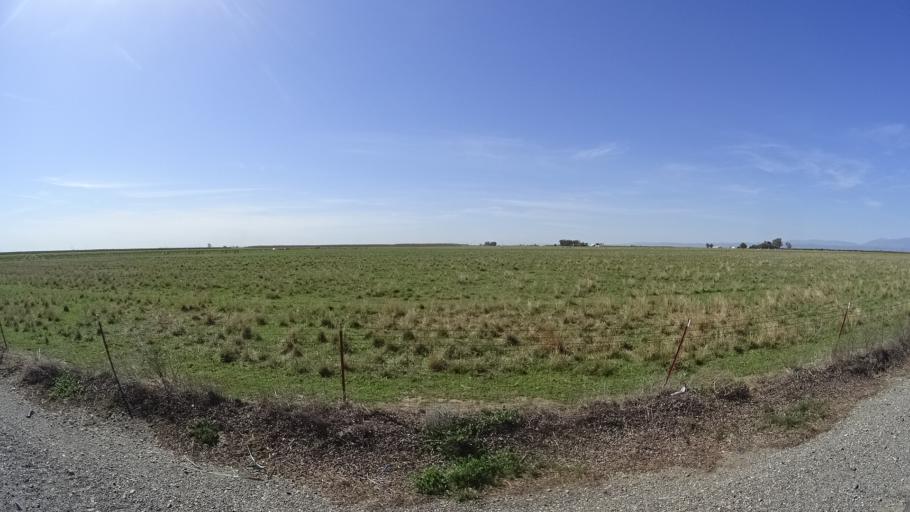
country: US
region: California
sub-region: Glenn County
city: Willows
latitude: 39.6238
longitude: -122.1457
